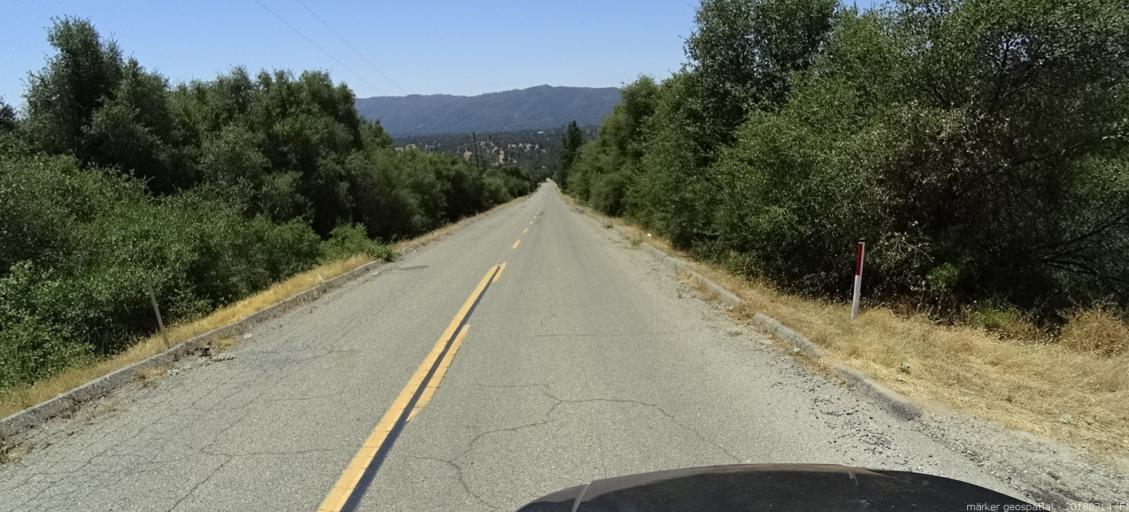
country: US
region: California
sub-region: Madera County
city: Ahwahnee
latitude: 37.3826
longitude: -119.7170
